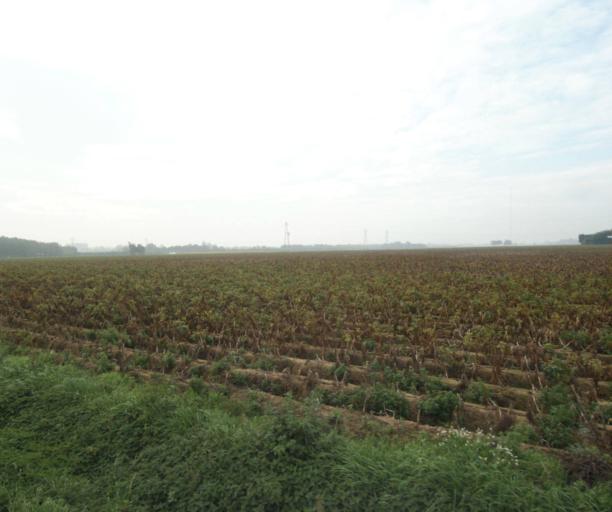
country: FR
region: Nord-Pas-de-Calais
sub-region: Departement du Nord
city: Phalempin
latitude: 50.5296
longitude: 3.0055
